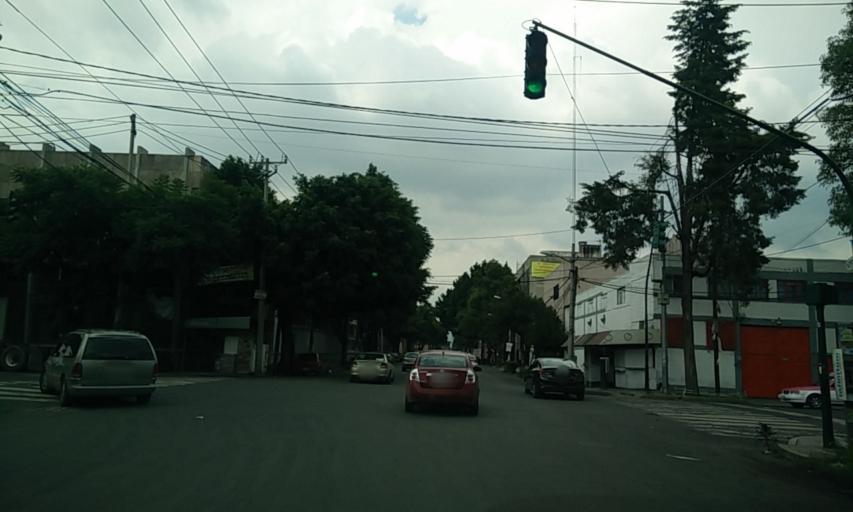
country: MX
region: Mexico City
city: Azcapotzalco
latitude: 19.4834
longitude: -99.1567
